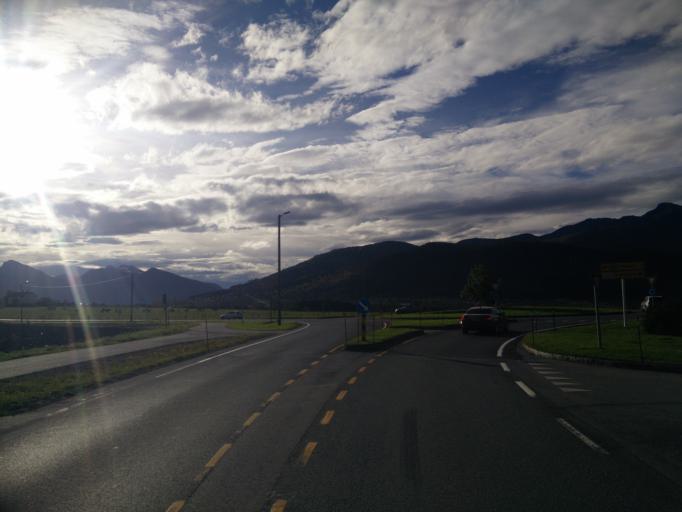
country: NO
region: More og Romsdal
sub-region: Vestnes
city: Vestnes
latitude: 62.6317
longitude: 7.0737
